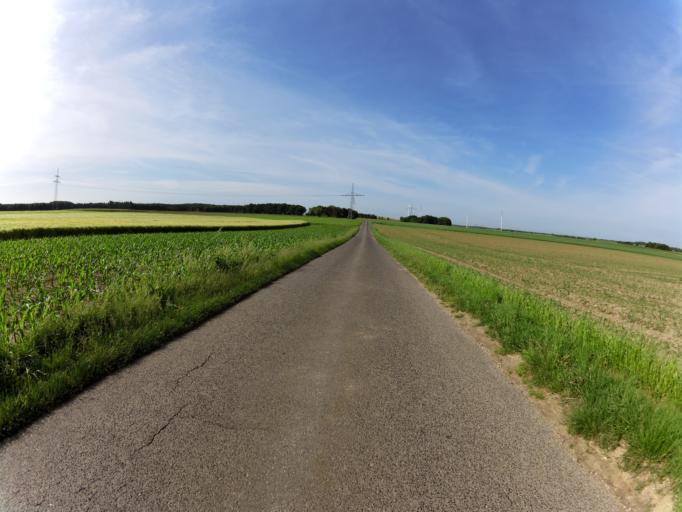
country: DE
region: North Rhine-Westphalia
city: Geilenkirchen
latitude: 51.0027
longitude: 6.0728
